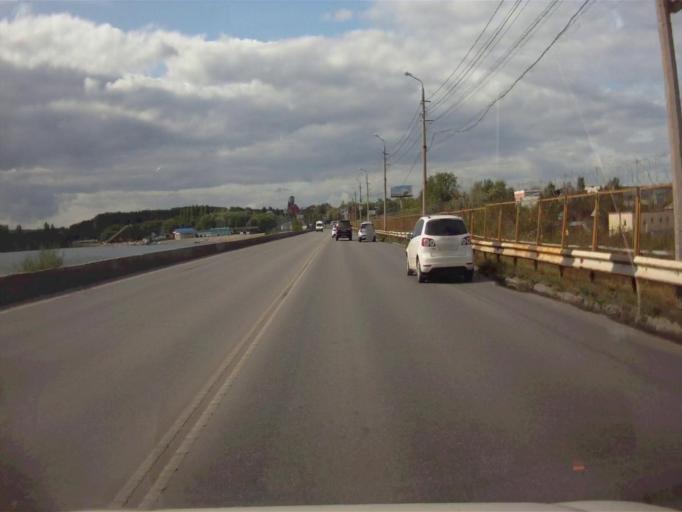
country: RU
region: Chelyabinsk
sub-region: Gorod Chelyabinsk
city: Chelyabinsk
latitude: 55.1468
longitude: 61.3078
